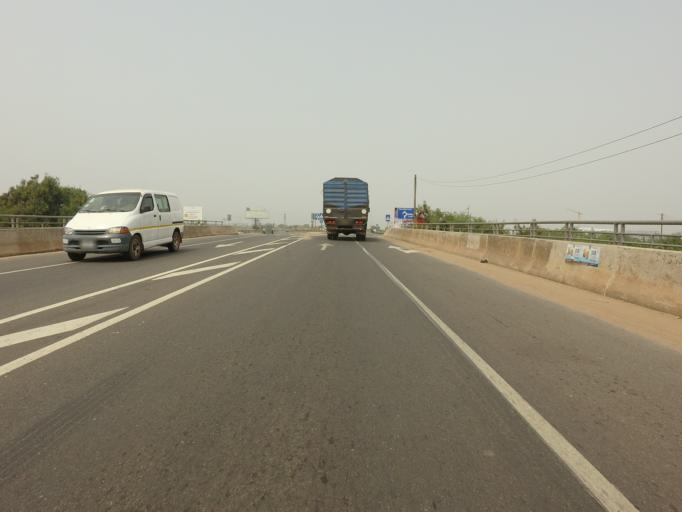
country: GH
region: Greater Accra
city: Nungua
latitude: 5.6569
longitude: -0.0763
